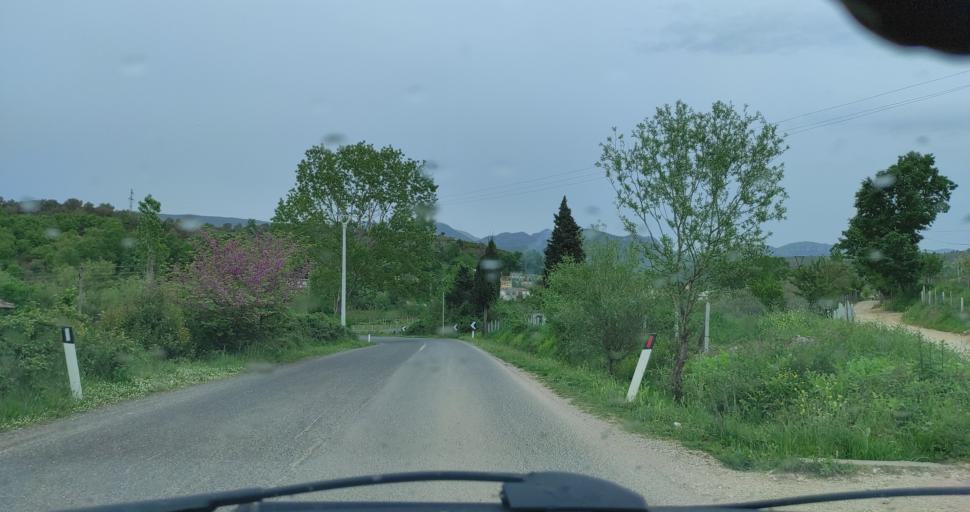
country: AL
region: Lezhe
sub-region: Rrethi i Kurbinit
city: Mamurras
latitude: 41.5890
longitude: 19.6981
